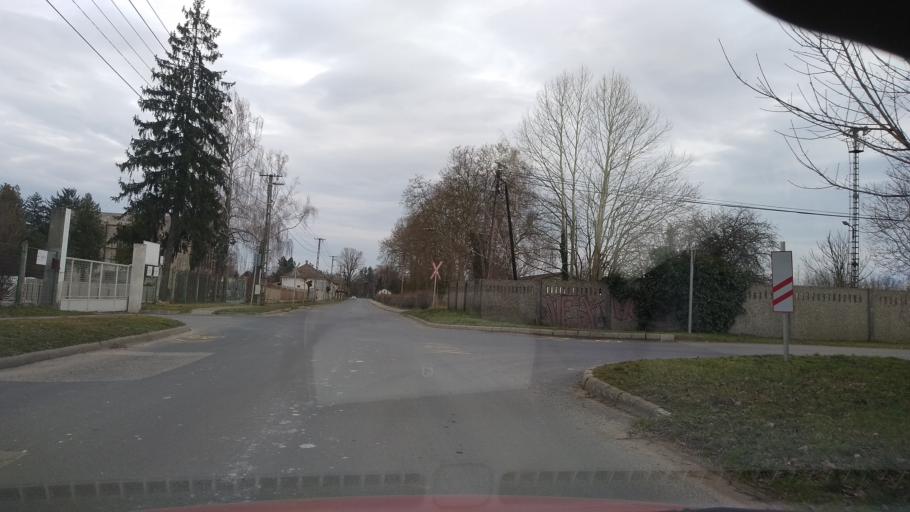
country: HU
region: Somogy
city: Barcs
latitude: 45.9532
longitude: 17.4423
